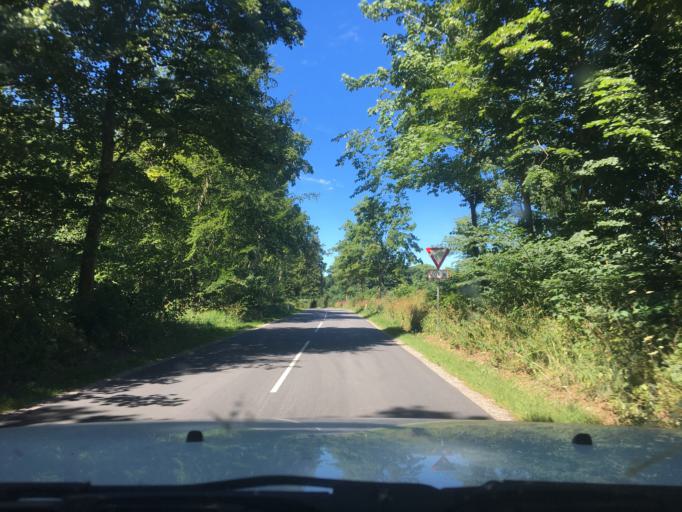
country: DK
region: Central Jutland
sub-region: Syddjurs Kommune
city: Hornslet
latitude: 56.3322
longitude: 10.3370
